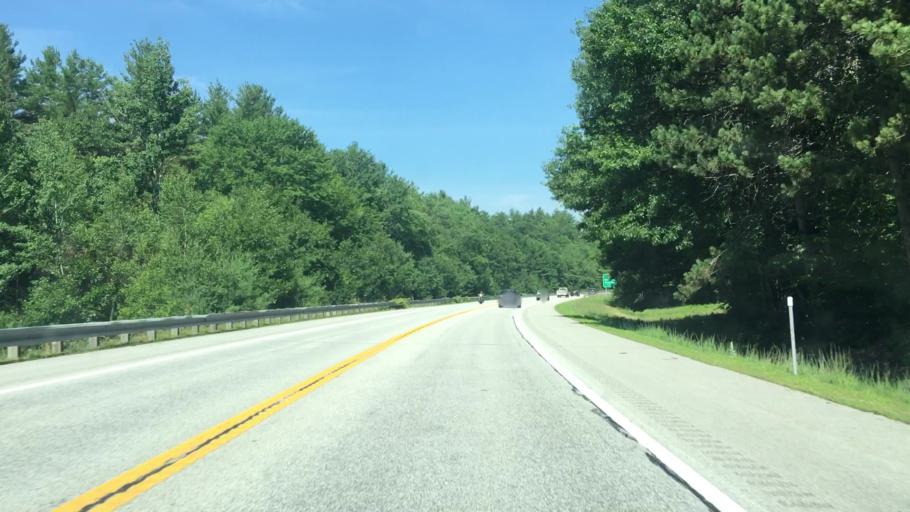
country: US
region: New Hampshire
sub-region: Merrimack County
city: Henniker
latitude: 43.1855
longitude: -71.8009
